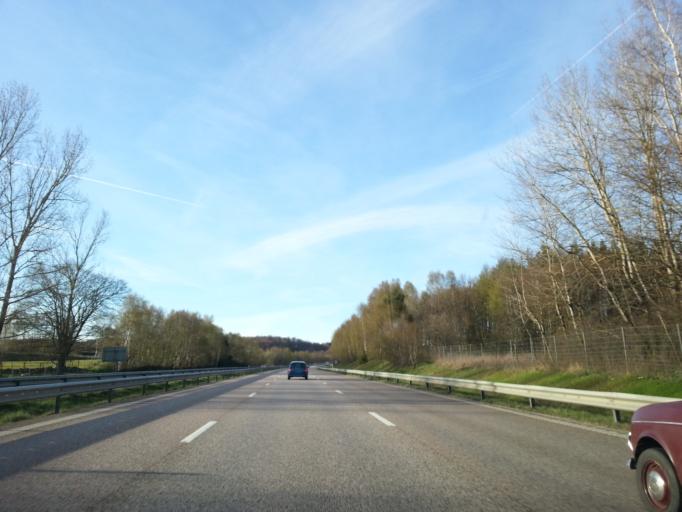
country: SE
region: Skane
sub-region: Angelholms Kommun
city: Munka-Ljungby
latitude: 56.3341
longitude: 12.9149
